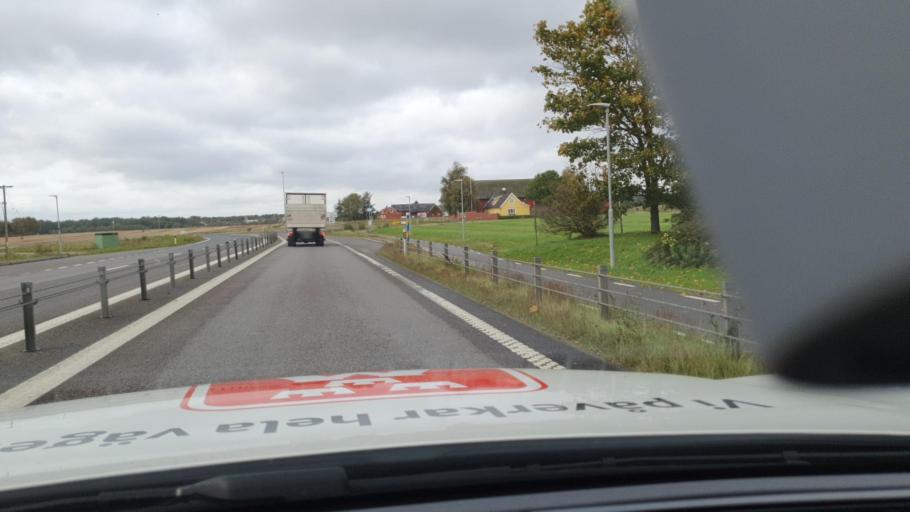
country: SE
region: Halland
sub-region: Laholms Kommun
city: Mellbystrand
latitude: 56.5037
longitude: 12.9827
